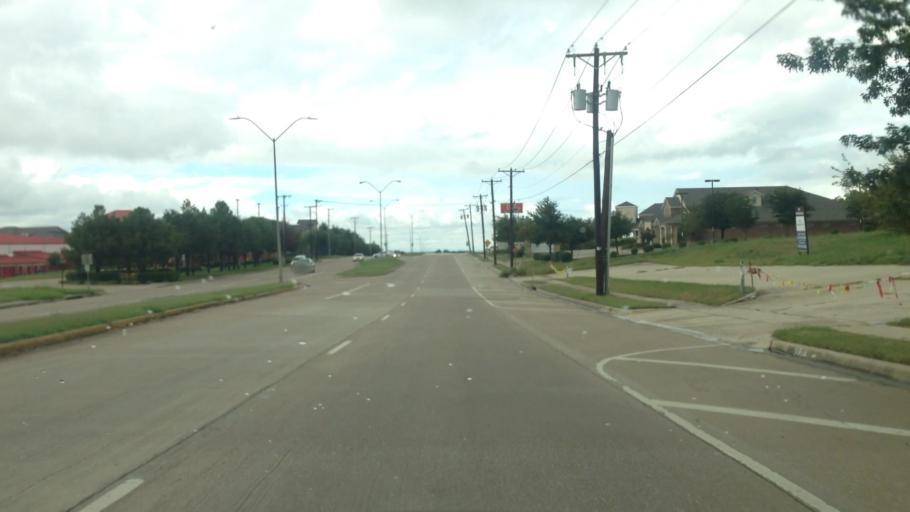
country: US
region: Texas
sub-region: Tarrant County
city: Benbrook
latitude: 32.6444
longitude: -97.4097
